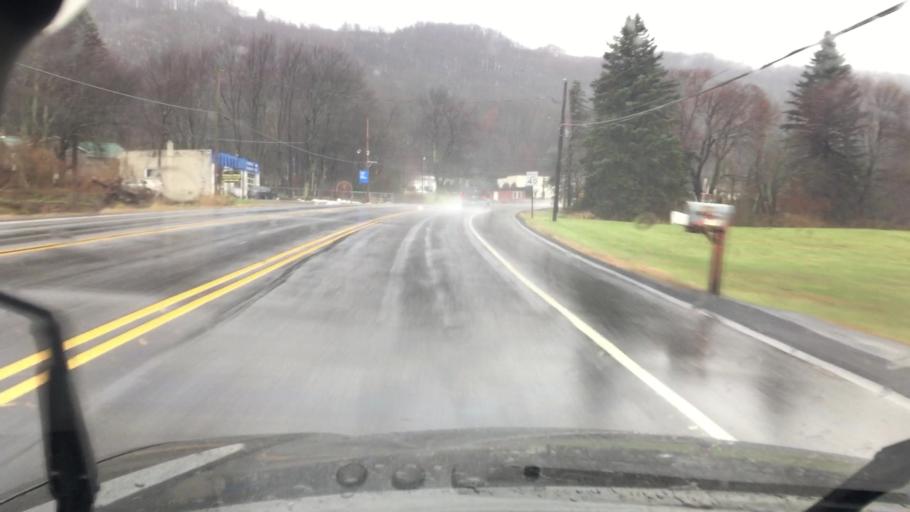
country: US
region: Pennsylvania
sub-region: Luzerne County
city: Harleigh
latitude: 41.0094
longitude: -75.9662
